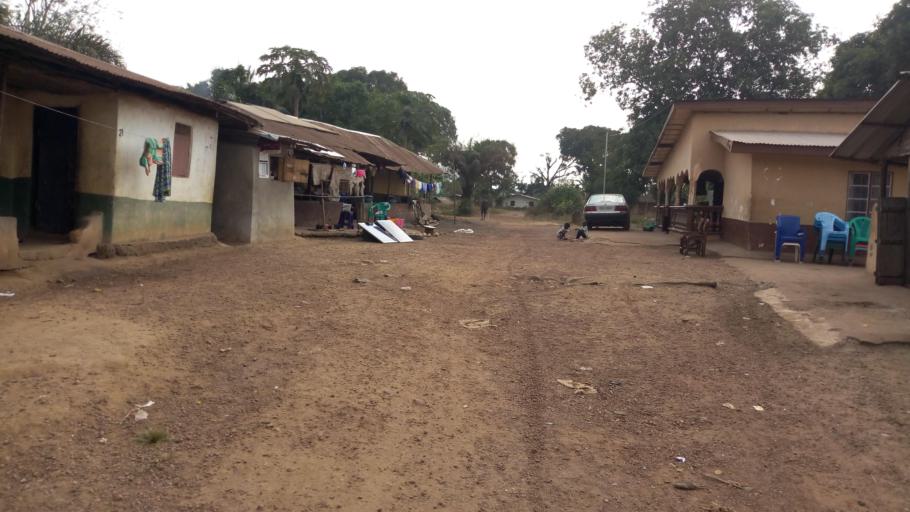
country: SL
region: Southern Province
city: Mogbwemo
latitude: 7.7645
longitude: -12.3123
